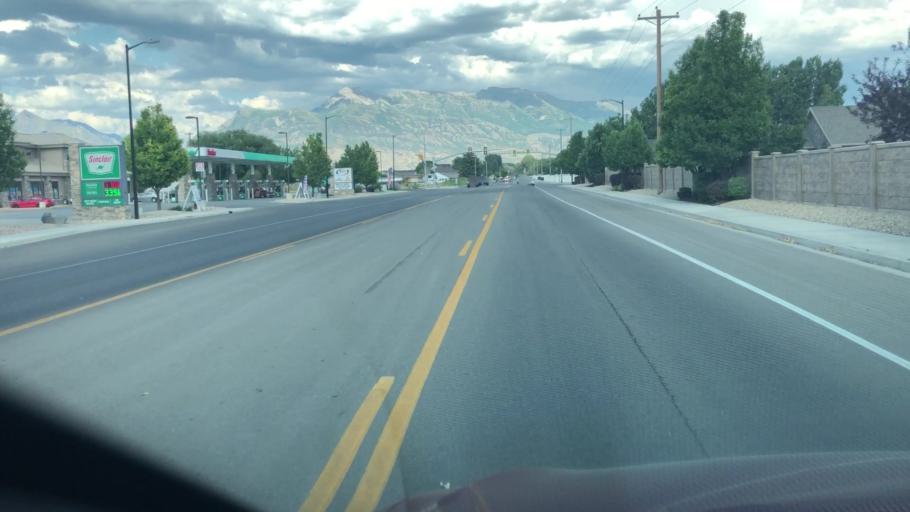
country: US
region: Utah
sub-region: Utah County
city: Lehi
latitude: 40.3872
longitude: -111.8786
